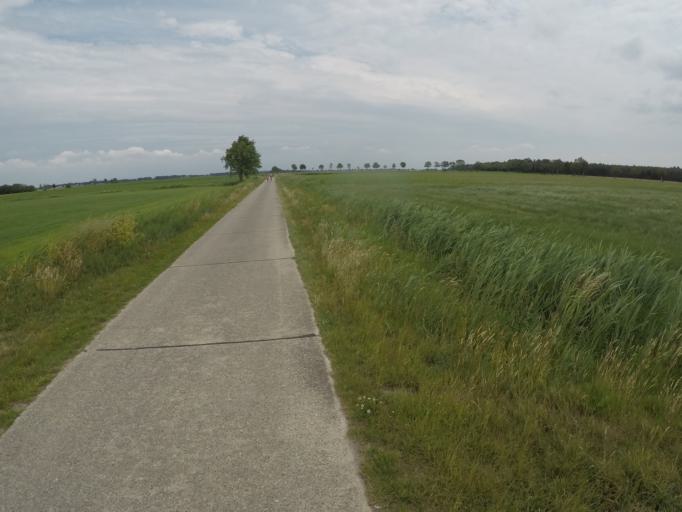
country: BE
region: Flanders
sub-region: Provincie Antwerpen
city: Wuustwezel
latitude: 51.4246
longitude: 4.5489
